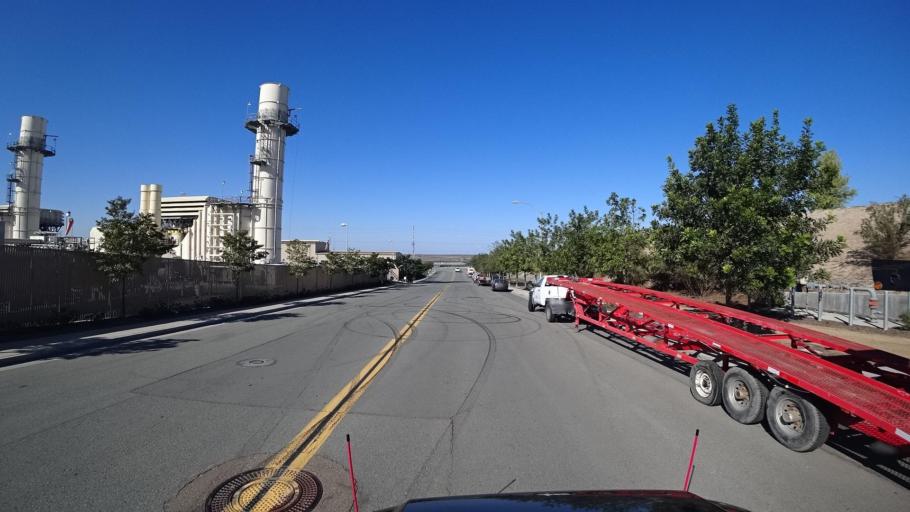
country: MX
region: Baja California
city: Tijuana
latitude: 32.5747
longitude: -116.9170
